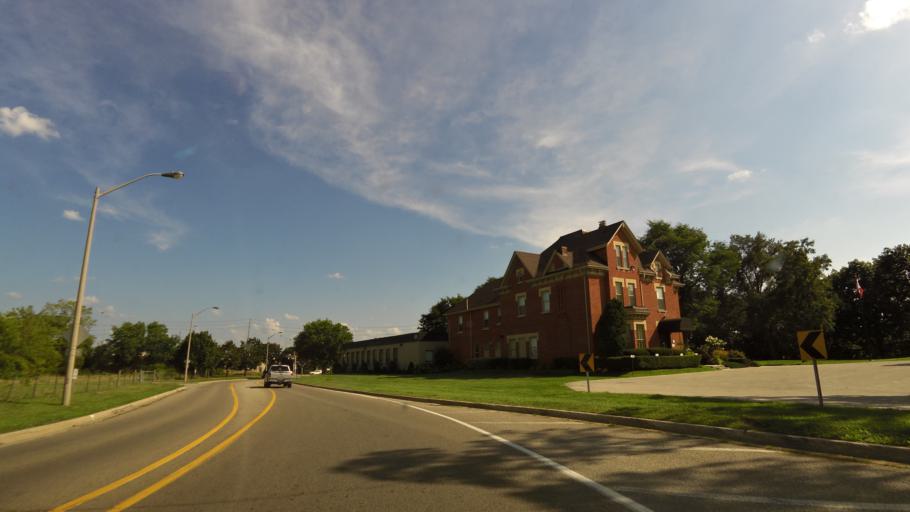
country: CA
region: Ontario
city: Burlington
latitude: 43.3292
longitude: -79.8248
